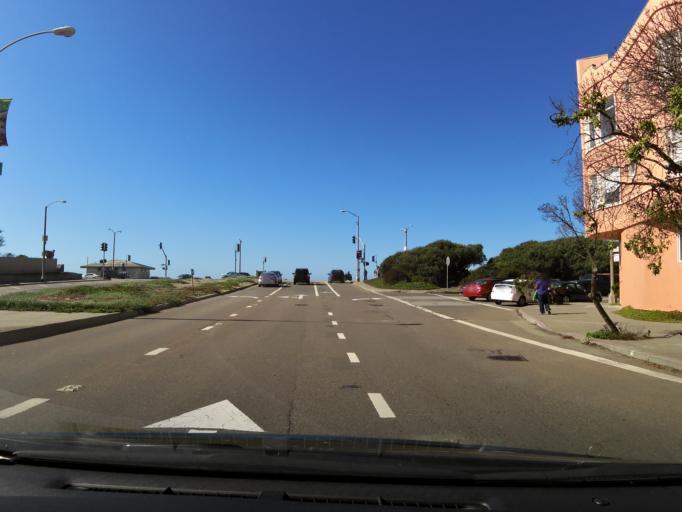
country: US
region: California
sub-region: San Mateo County
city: Daly City
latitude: 37.7355
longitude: -122.5057
